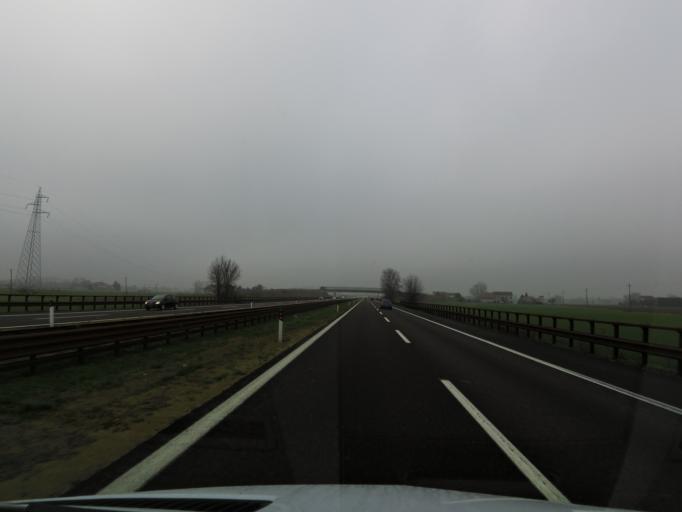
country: IT
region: Lombardy
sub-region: Provincia di Mantova
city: Pegognaga
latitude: 45.0098
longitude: 10.8507
